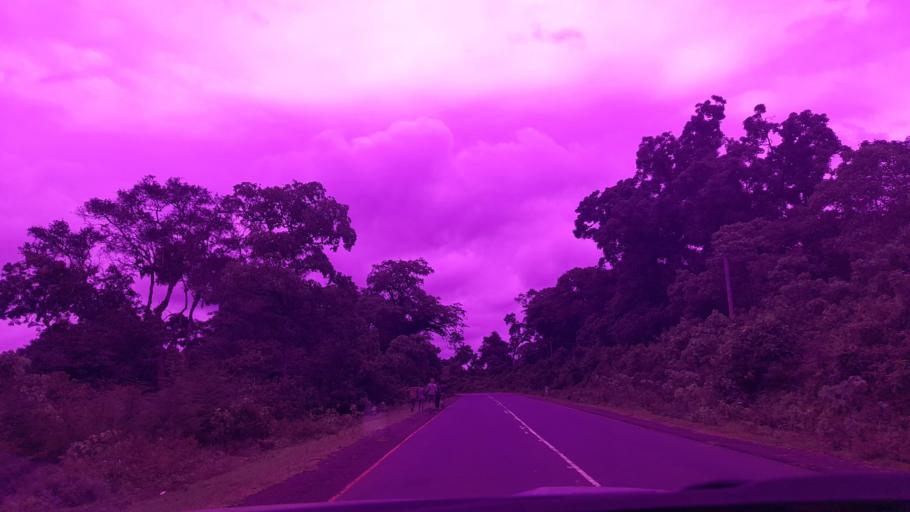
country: ET
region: Southern Nations, Nationalities, and People's Region
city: Bonga
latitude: 7.2814
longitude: 35.9650
